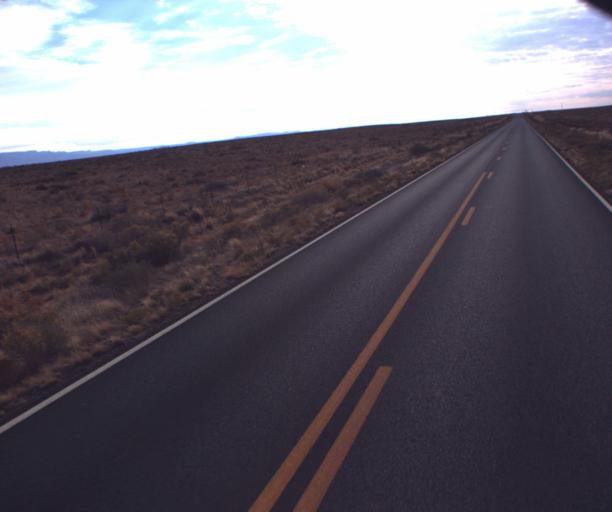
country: US
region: Arizona
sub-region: Apache County
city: Many Farms
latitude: 36.5581
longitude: -109.5376
